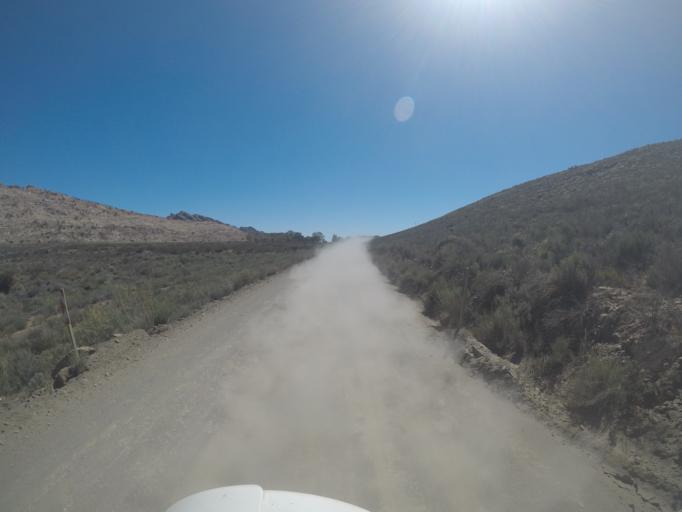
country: ZA
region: Western Cape
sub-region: Cape Winelands District Municipality
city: Ceres
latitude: -32.8191
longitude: 19.4523
